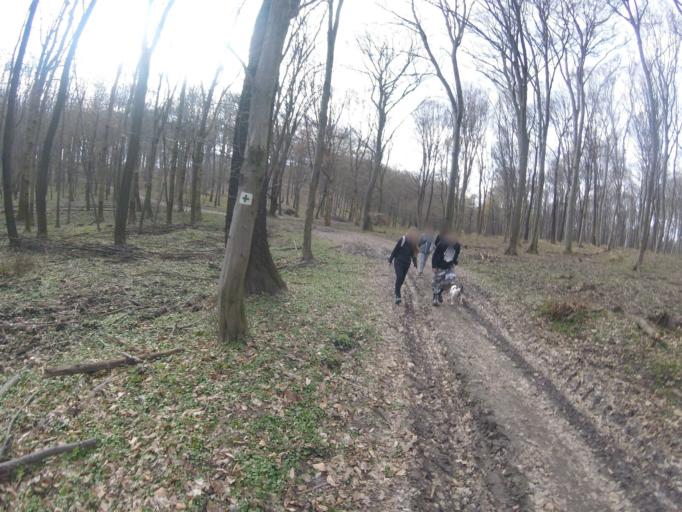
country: HU
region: Fejer
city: Szarliget
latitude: 47.4858
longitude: 18.4191
